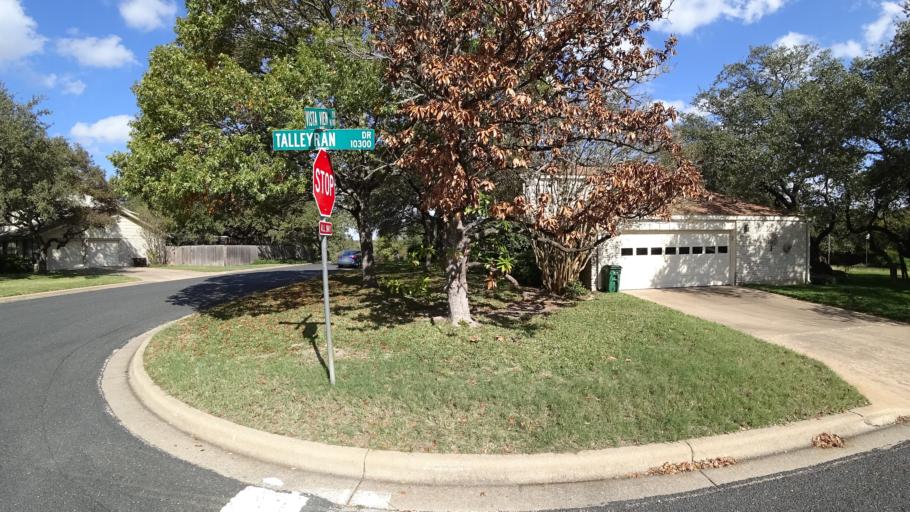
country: US
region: Texas
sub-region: Williamson County
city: Anderson Mill
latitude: 30.4274
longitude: -97.8041
